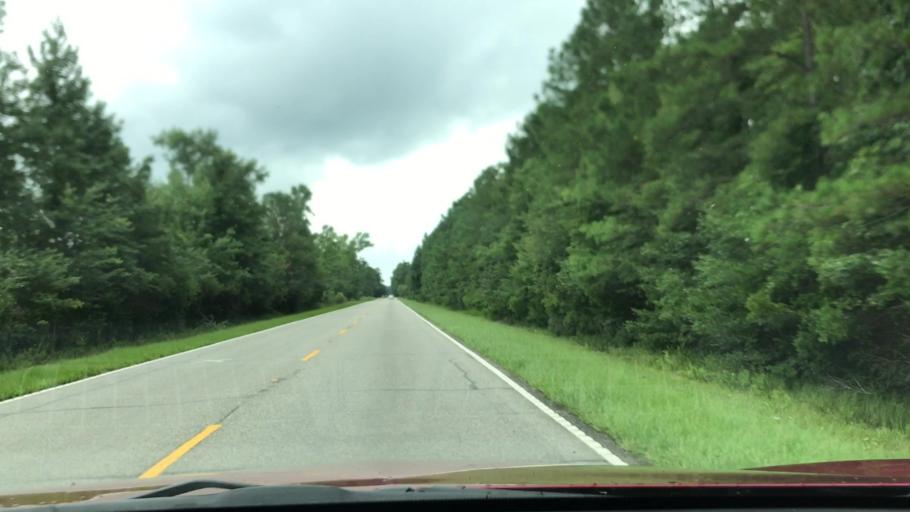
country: US
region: South Carolina
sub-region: Georgetown County
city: Georgetown
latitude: 33.5371
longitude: -79.2325
